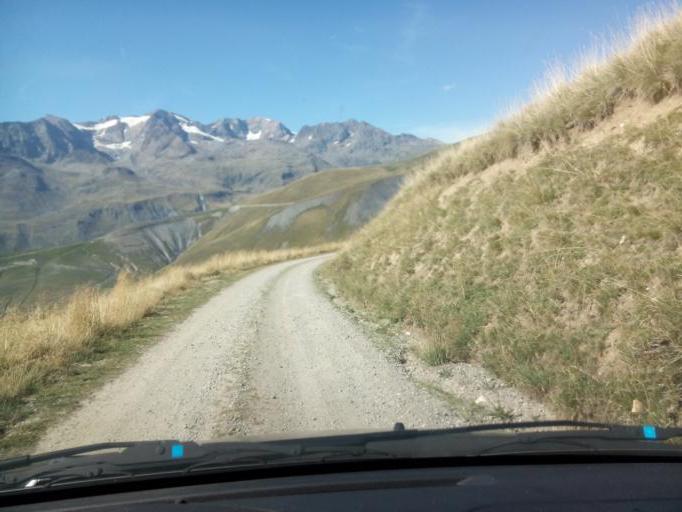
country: FR
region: Rhone-Alpes
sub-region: Departement de l'Isere
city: Mont-de-Lans
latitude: 45.0717
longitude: 6.1977
